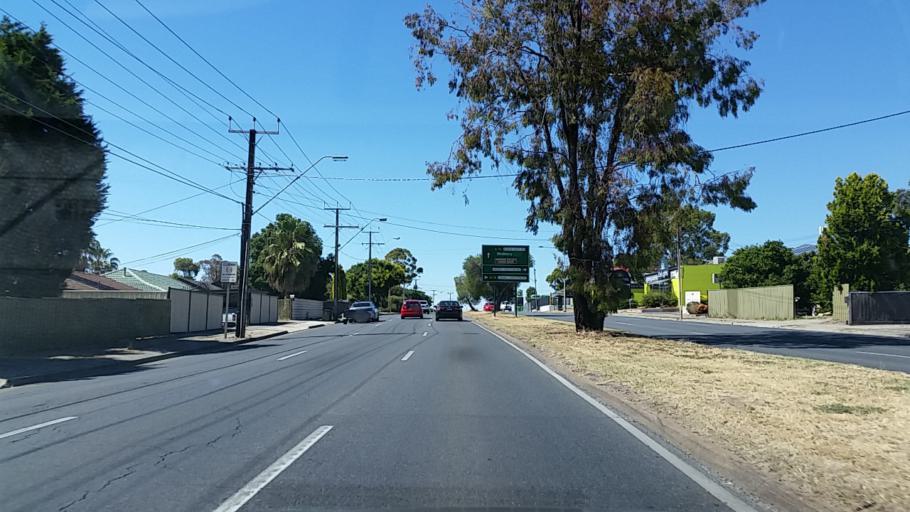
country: AU
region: South Australia
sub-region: Port Adelaide Enfield
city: Gilles Plains
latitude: -34.8480
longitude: 138.6698
